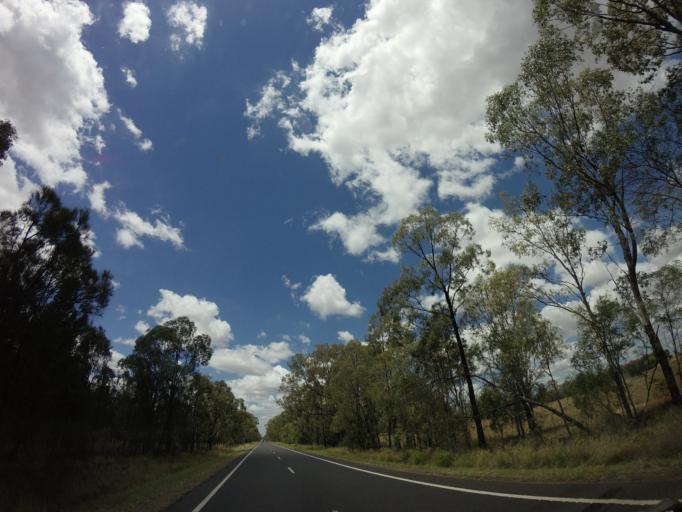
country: AU
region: Queensland
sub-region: Toowoomba
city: Oakey
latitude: -27.9002
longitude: 151.1995
